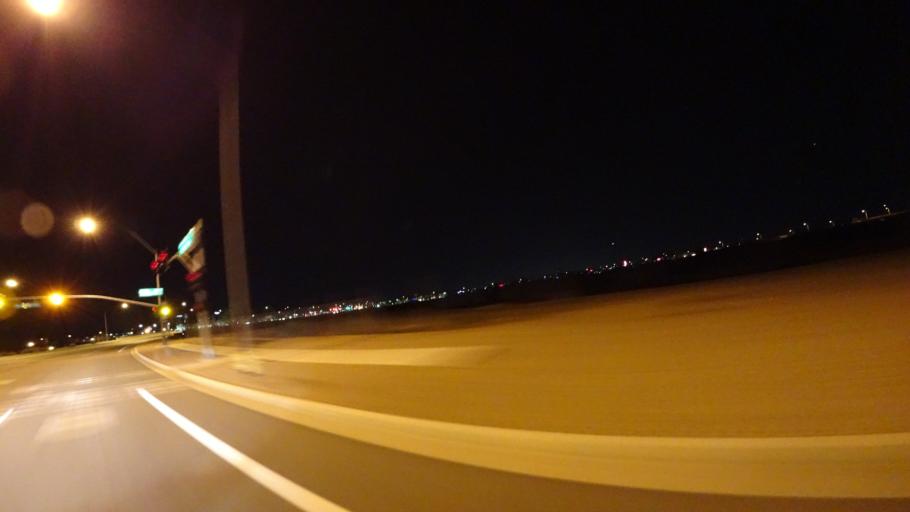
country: US
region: Arizona
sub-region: Maricopa County
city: Queen Creek
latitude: 33.3228
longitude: -111.6805
